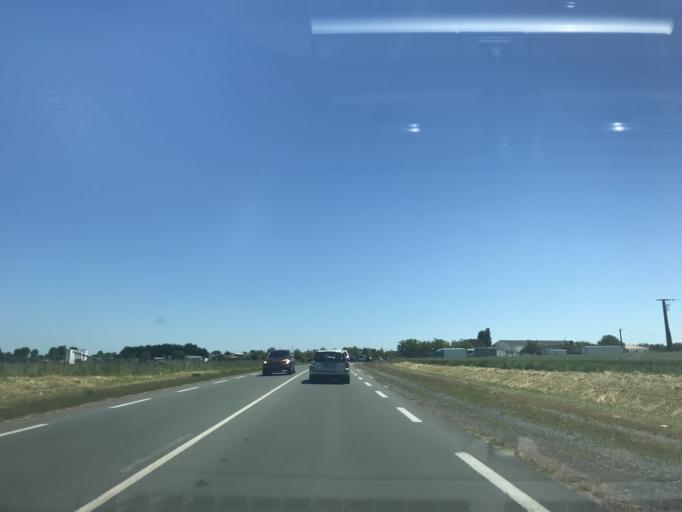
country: FR
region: Poitou-Charentes
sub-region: Departement de la Charente-Maritime
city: Saint-Georges-de-Didonne
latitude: 45.6103
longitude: -0.9782
